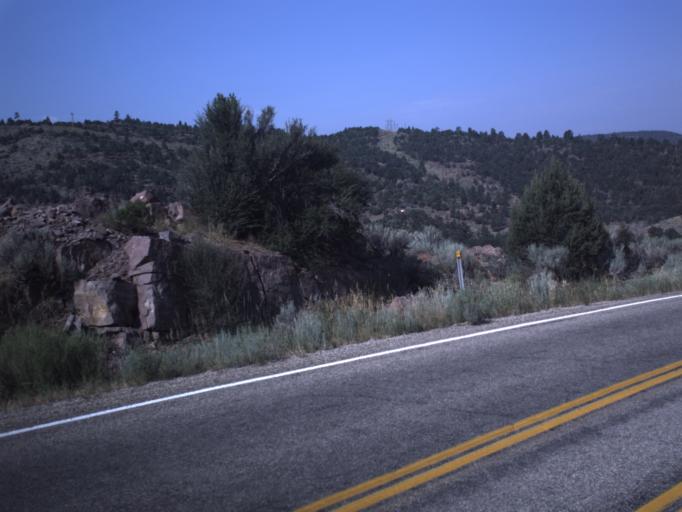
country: US
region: Utah
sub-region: Daggett County
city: Manila
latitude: 40.9112
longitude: -109.4168
